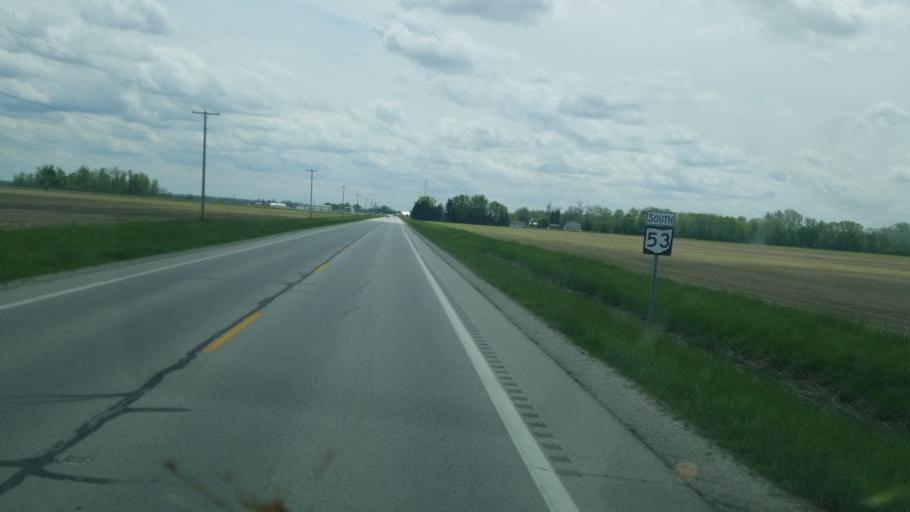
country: US
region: Ohio
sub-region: Sandusky County
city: Ballville
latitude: 41.2449
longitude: -83.1679
